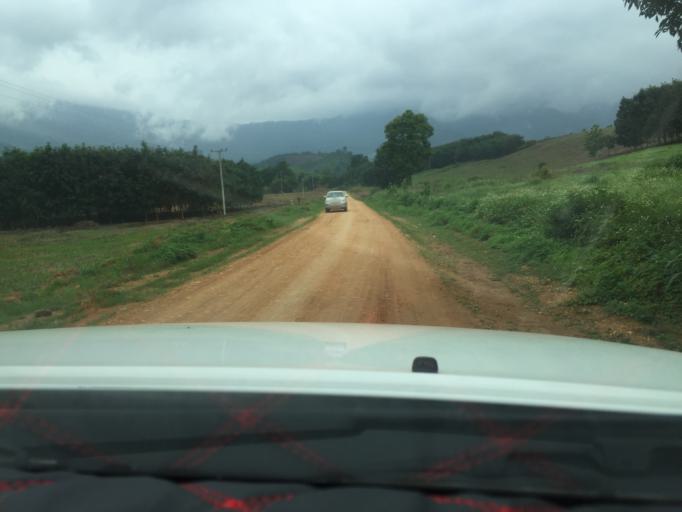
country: TH
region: Phayao
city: Phu Sang
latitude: 19.7414
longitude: 100.4597
